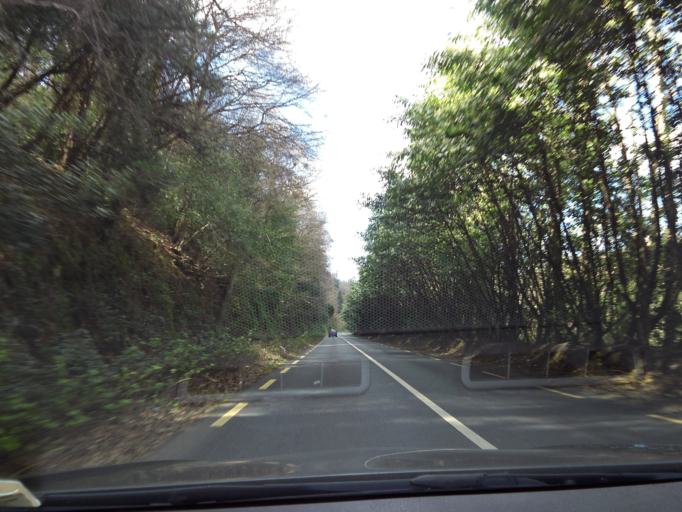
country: IE
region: Leinster
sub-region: Wicklow
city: Arklow
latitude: 52.8124
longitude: -6.1940
